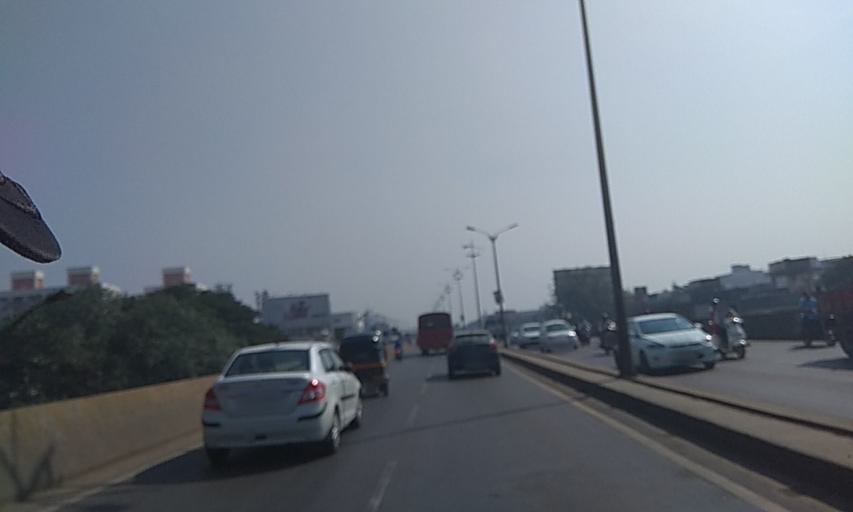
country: IN
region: Maharashtra
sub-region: Pune Division
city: Pune
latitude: 18.5012
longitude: 73.9356
